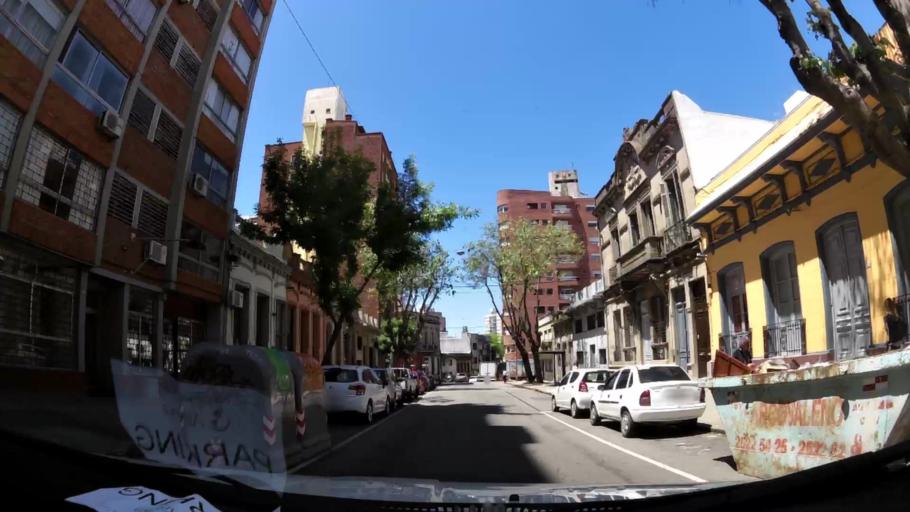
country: UY
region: Montevideo
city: Montevideo
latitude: -34.9042
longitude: -56.1750
